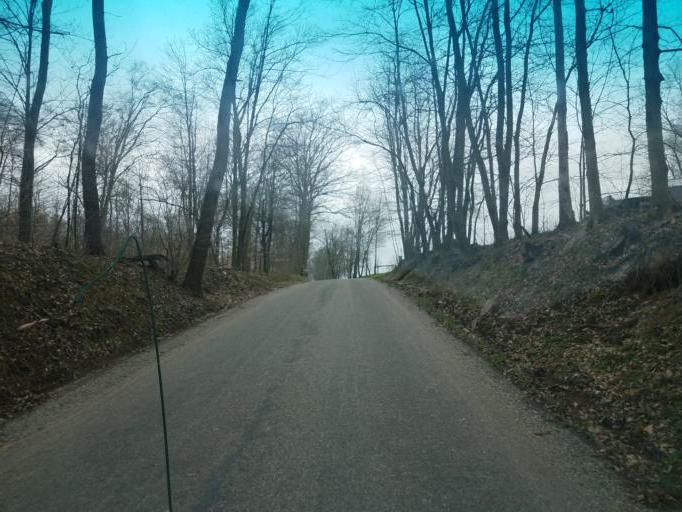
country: US
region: Ohio
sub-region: Stark County
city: Beach City
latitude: 40.6259
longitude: -81.7212
